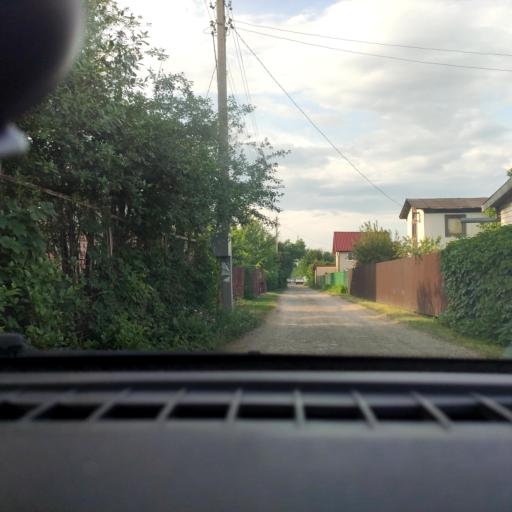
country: RU
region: Samara
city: Tol'yatti
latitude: 53.5910
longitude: 49.3199
